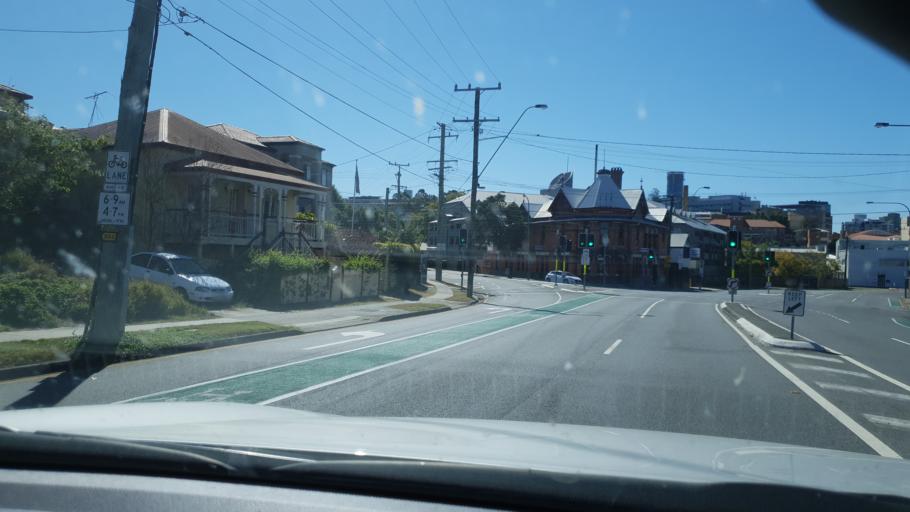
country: AU
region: Queensland
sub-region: Brisbane
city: Woolloongabba
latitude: -27.4906
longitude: 153.0271
